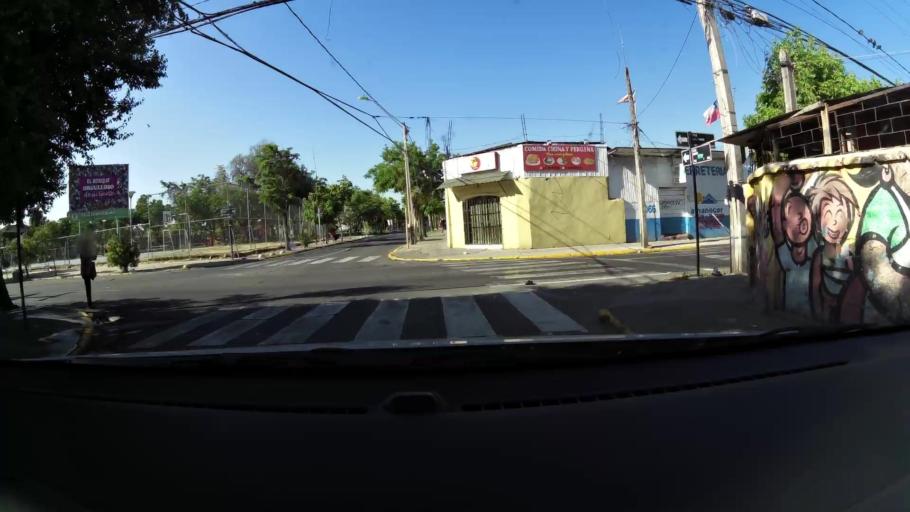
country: CL
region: Santiago Metropolitan
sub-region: Provincia de Maipo
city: San Bernardo
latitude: -33.5489
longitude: -70.6842
